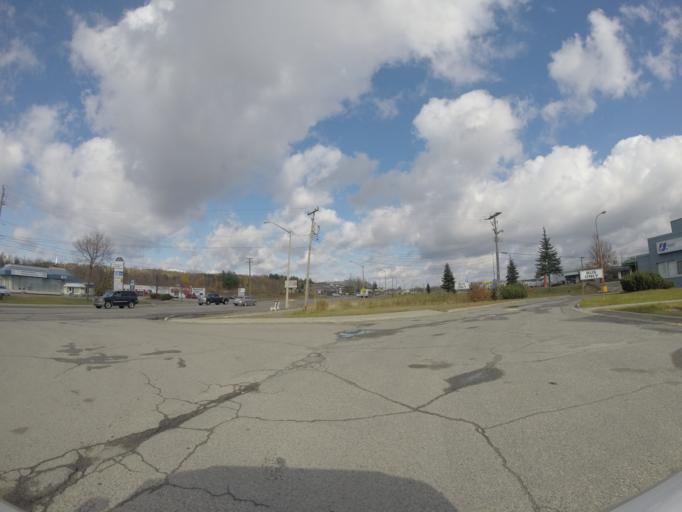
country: CA
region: Ontario
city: Greater Sudbury
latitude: 46.5119
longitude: -80.9857
